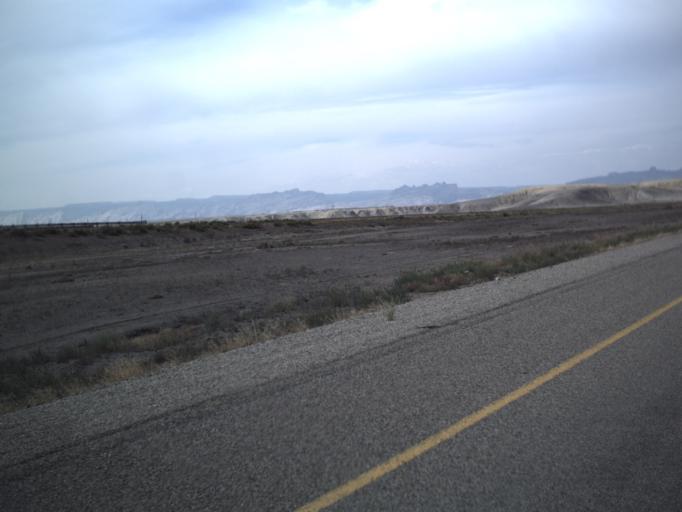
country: US
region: Utah
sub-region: Carbon County
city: East Carbon City
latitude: 38.9836
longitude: -110.2330
